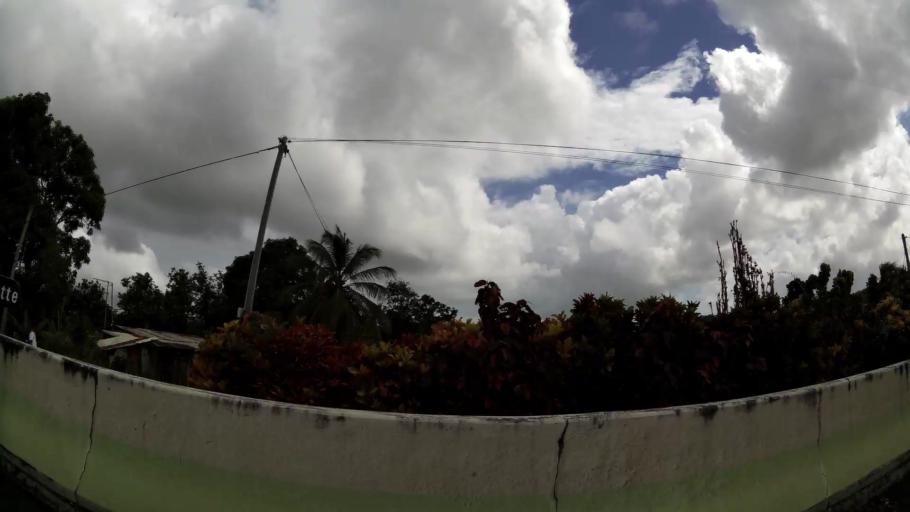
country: MQ
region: Martinique
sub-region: Martinique
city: Ducos
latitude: 14.5690
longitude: -60.9797
